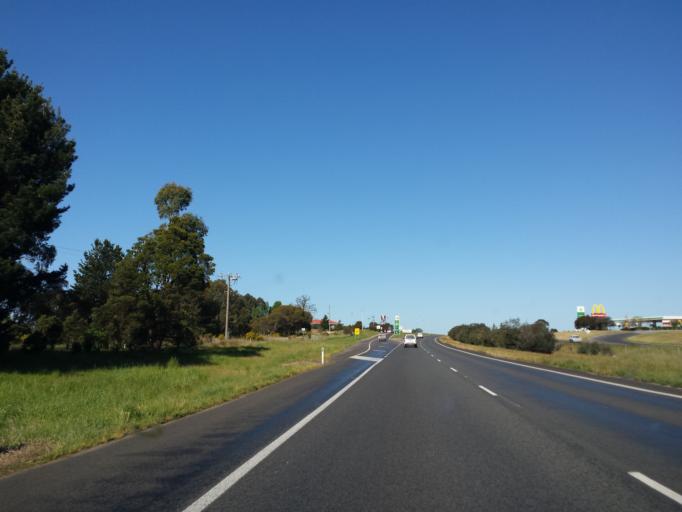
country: AU
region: Victoria
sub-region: Moorabool
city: Bacchus Marsh
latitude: -37.5905
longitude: 144.2391
